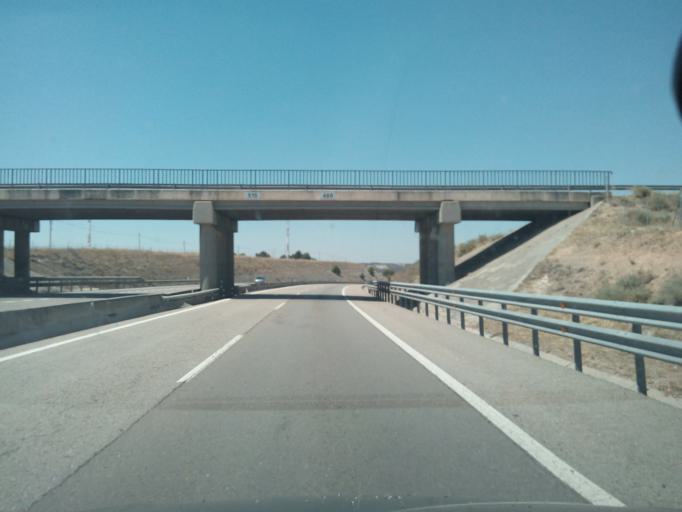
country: ES
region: Castille-La Mancha
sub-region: Province of Toledo
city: Tembleque
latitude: 39.7821
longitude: -3.4816
